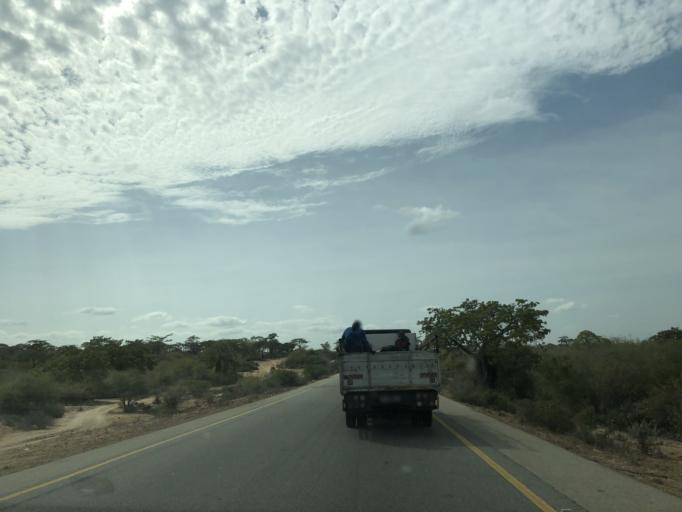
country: AO
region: Benguela
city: Benguela
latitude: -13.0069
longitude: 13.7077
